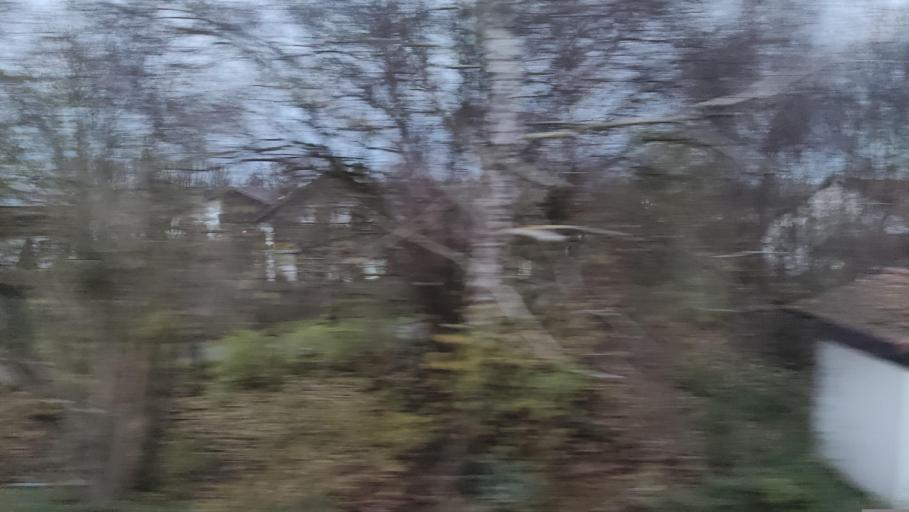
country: DE
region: Bavaria
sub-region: Upper Bavaria
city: Rattenkirchen
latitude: 48.2553
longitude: 12.3446
